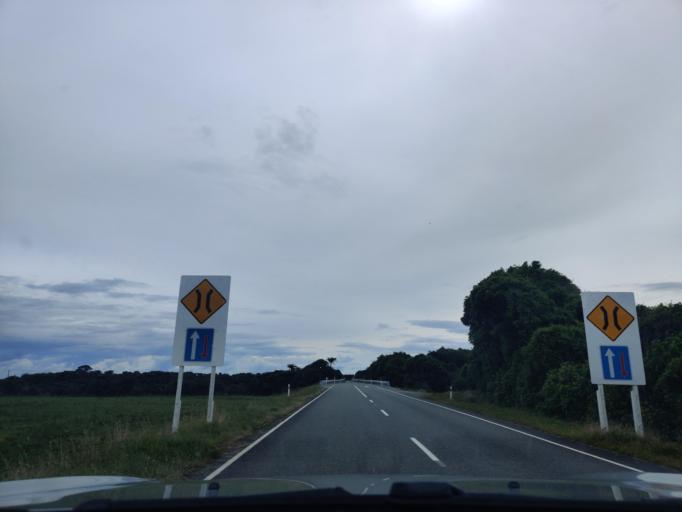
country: NZ
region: West Coast
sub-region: Westland District
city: Hokitika
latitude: -42.9107
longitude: 170.7676
